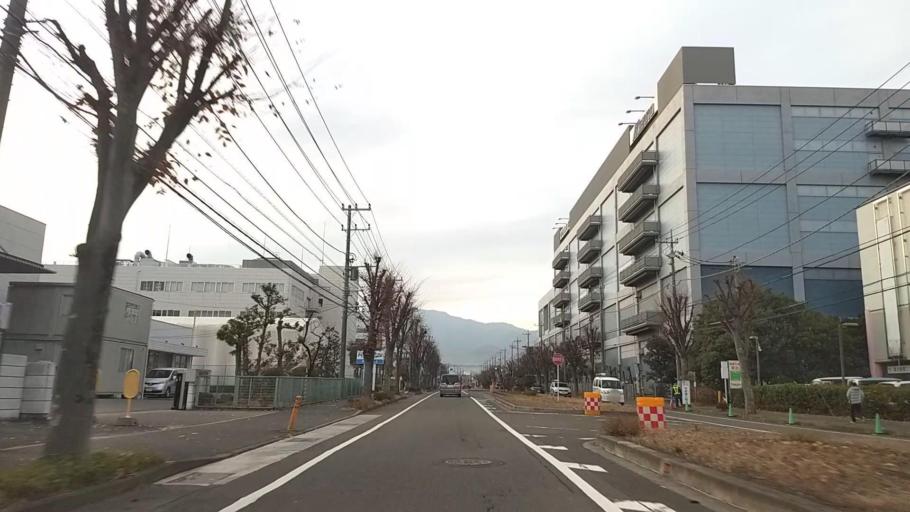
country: JP
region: Kanagawa
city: Atsugi
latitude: 35.4276
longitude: 139.3433
